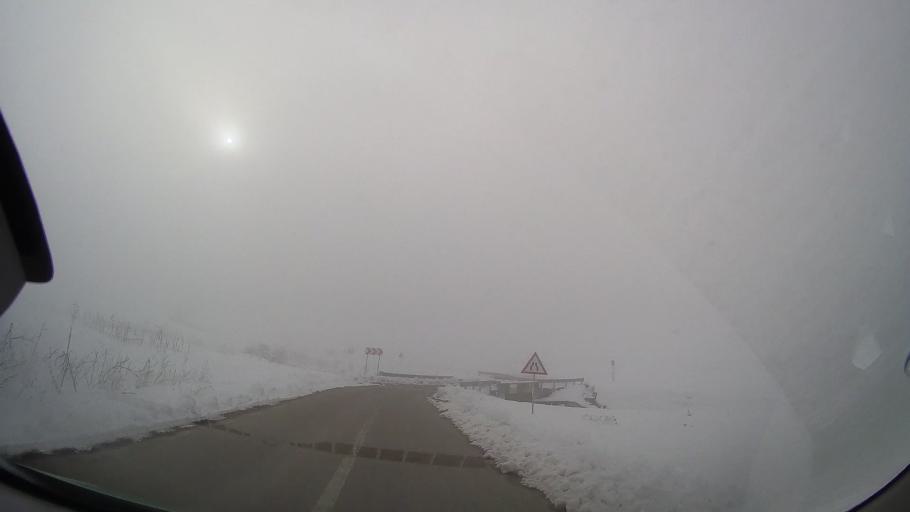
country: RO
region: Iasi
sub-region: Comuna Valea Seaca
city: Topile
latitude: 47.2710
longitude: 26.6698
